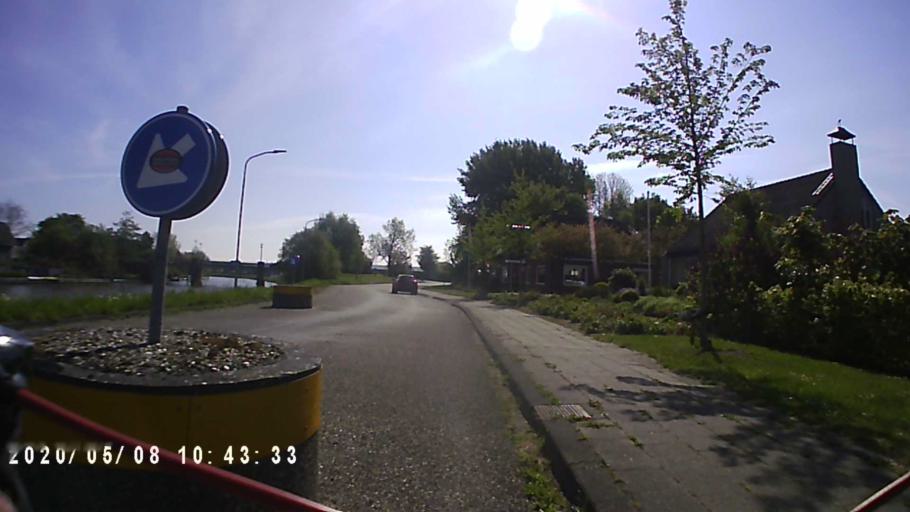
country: NL
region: Groningen
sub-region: Gemeente Winsum
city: Winsum
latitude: 53.3329
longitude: 6.5243
